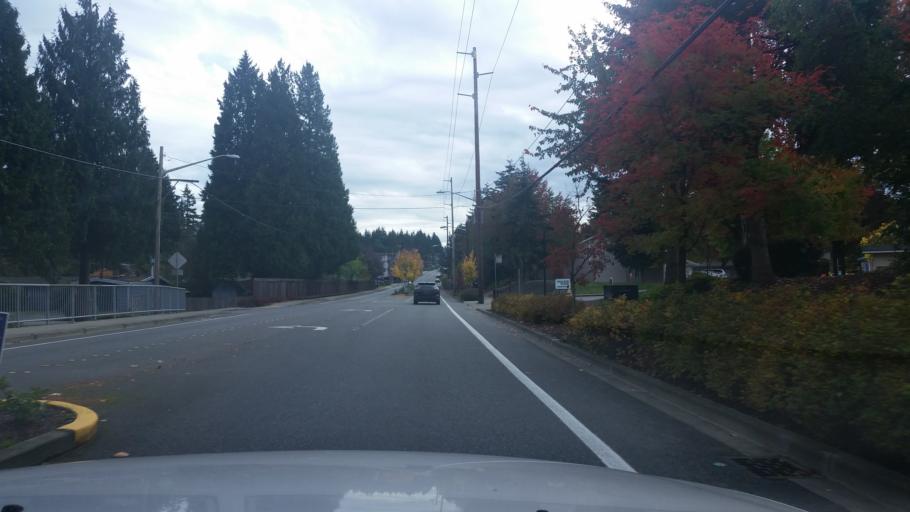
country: US
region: Washington
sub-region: King County
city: Eastgate
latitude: 47.5996
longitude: -122.1524
